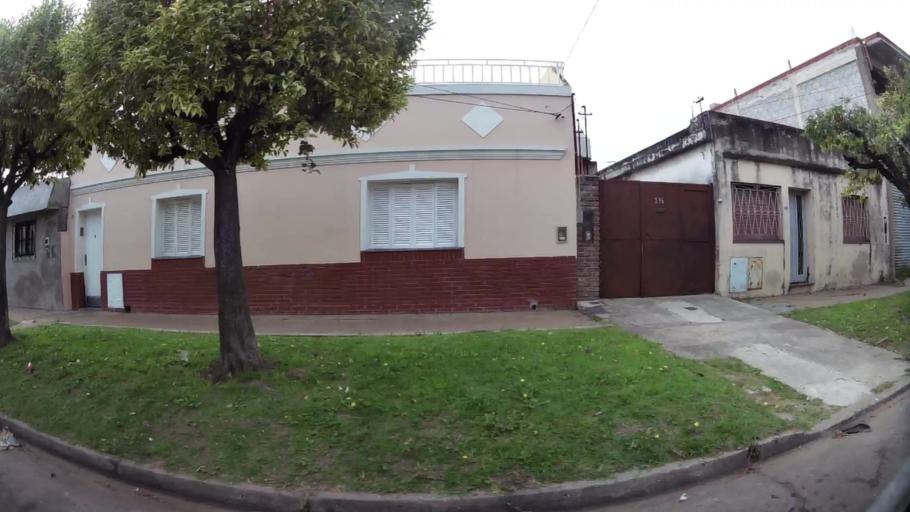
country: AR
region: Buenos Aires F.D.
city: Villa Lugano
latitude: -34.6959
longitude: -58.5134
